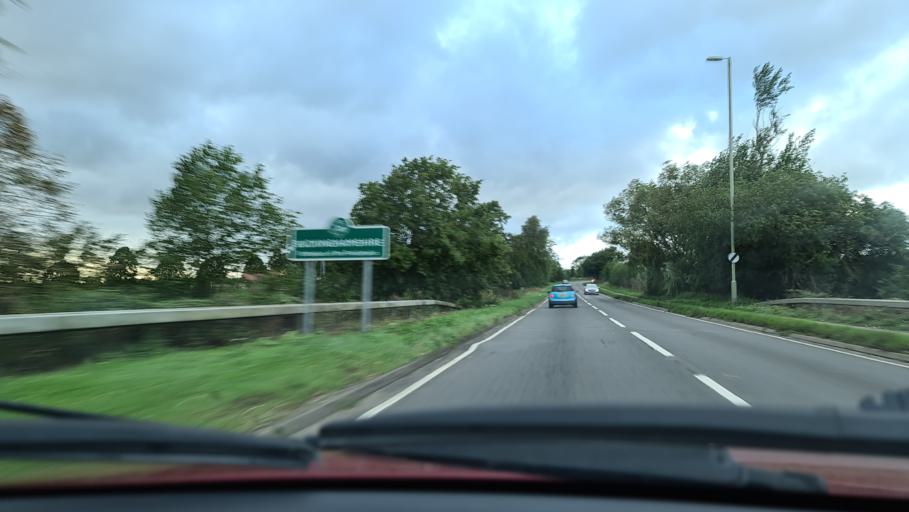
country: GB
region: England
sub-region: Oxfordshire
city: Thame
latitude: 51.7570
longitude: -0.9811
